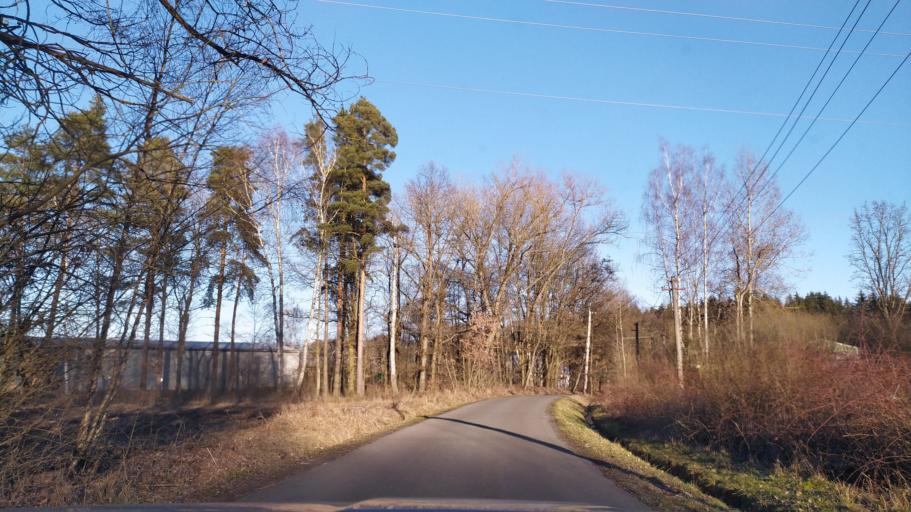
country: CZ
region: Karlovarsky
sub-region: Okres Cheb
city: Frantiskovy Lazne
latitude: 50.1114
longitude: 12.3095
